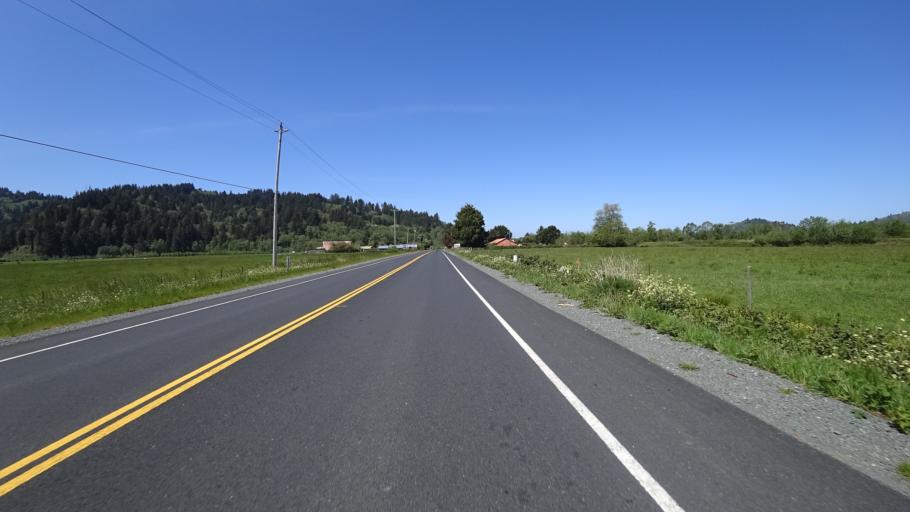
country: US
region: California
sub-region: Humboldt County
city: Westhaven-Moonstone
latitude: 41.2846
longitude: -124.0679
